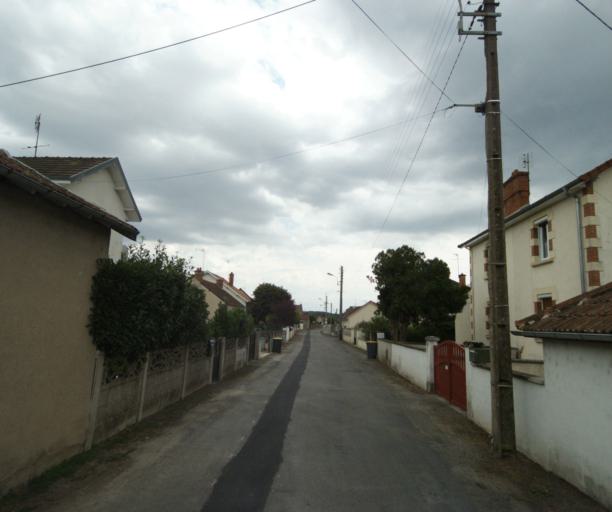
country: FR
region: Bourgogne
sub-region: Departement de Saone-et-Loire
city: Gueugnon
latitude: 46.6024
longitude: 4.0505
